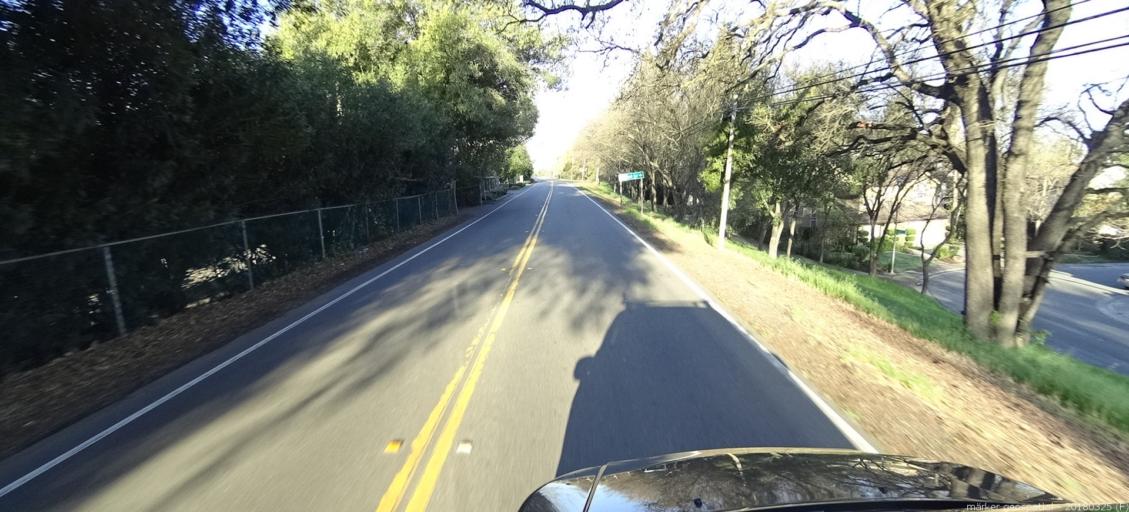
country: US
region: California
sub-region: Yolo County
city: West Sacramento
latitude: 38.6056
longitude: -121.5271
